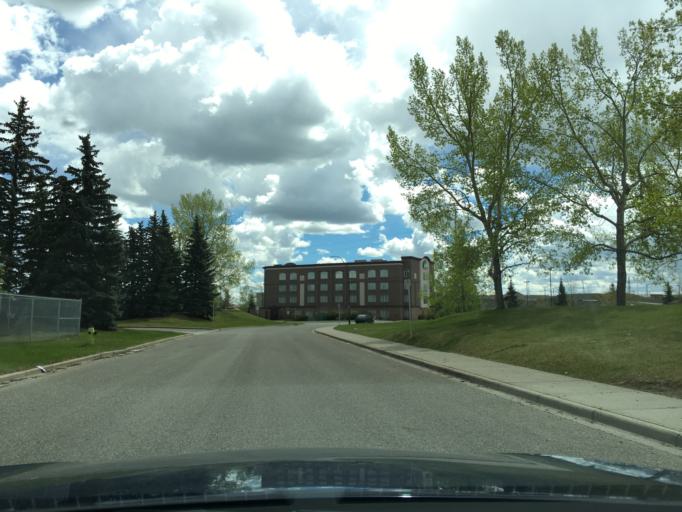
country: CA
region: Alberta
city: Calgary
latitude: 50.9077
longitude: -114.0619
